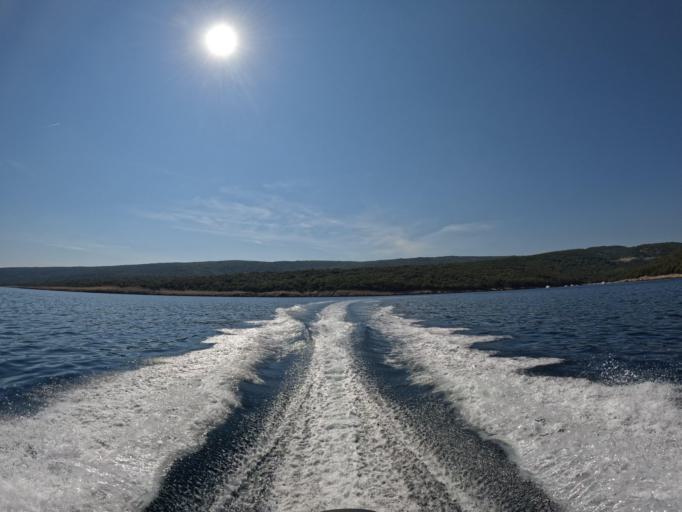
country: HR
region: Primorsko-Goranska
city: Cres
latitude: 44.9461
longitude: 14.4699
